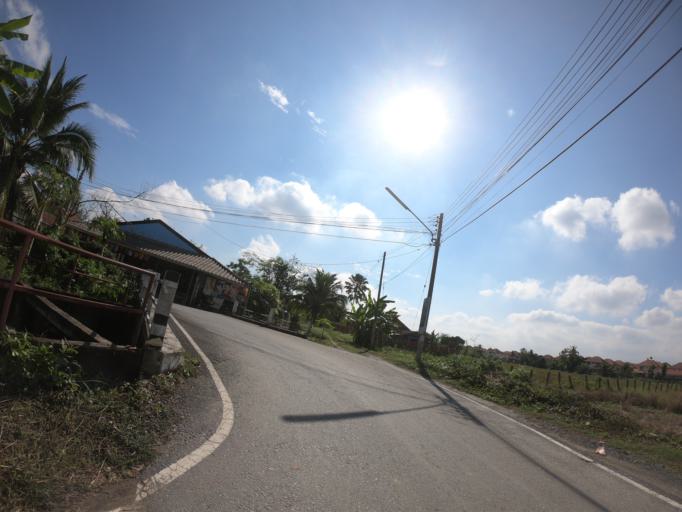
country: TH
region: Chiang Mai
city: San Sai
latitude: 18.8429
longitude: 99.0590
